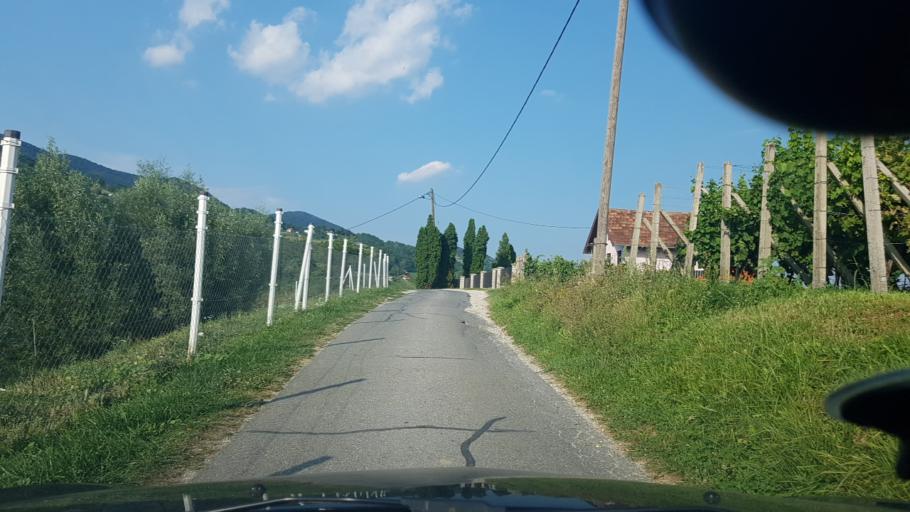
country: HR
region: Krapinsko-Zagorska
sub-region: Grad Krapina
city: Krapina
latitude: 46.1628
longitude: 15.8932
